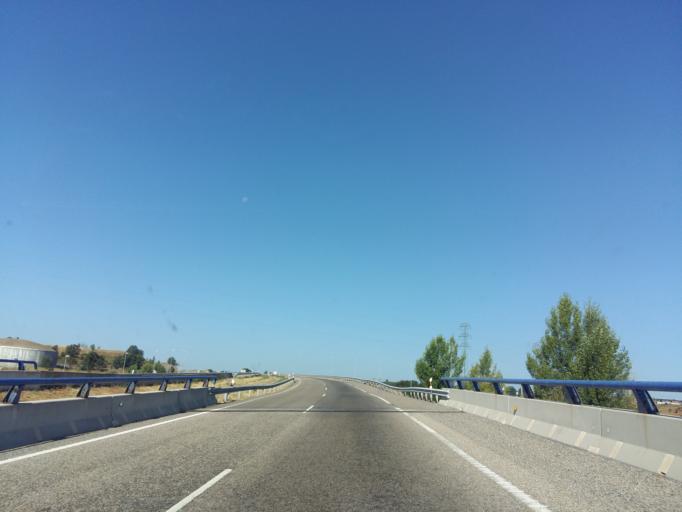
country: ES
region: Castille and Leon
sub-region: Provincia de Leon
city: San Andres del Rabanedo
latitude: 42.5767
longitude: -5.6212
